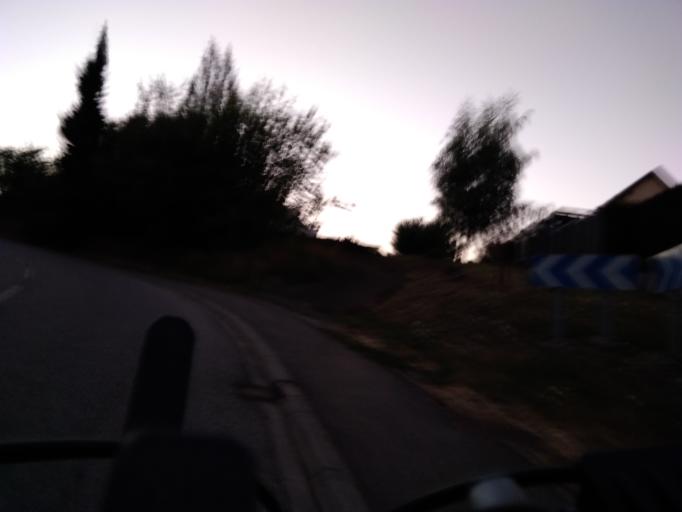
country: FR
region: Lorraine
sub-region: Departement de la Moselle
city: Neufgrange
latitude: 49.0784
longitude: 7.0570
